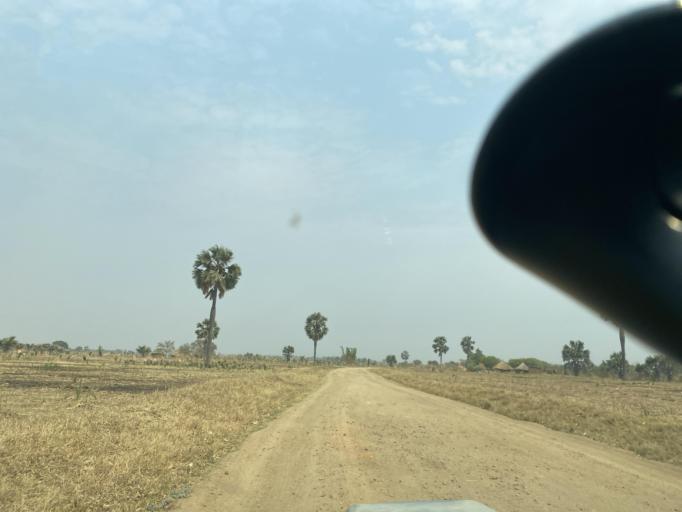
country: ZM
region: Lusaka
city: Kafue
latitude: -15.6515
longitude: 28.0511
